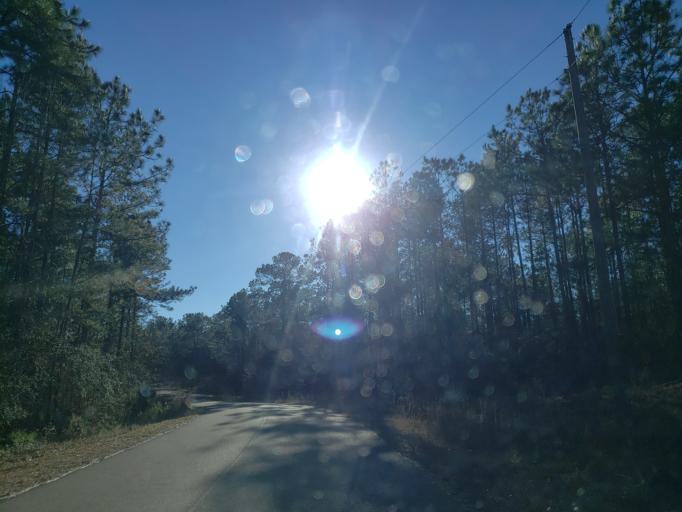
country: US
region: Mississippi
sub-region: Lamar County
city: Sumrall
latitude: 31.3606
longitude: -89.4751
